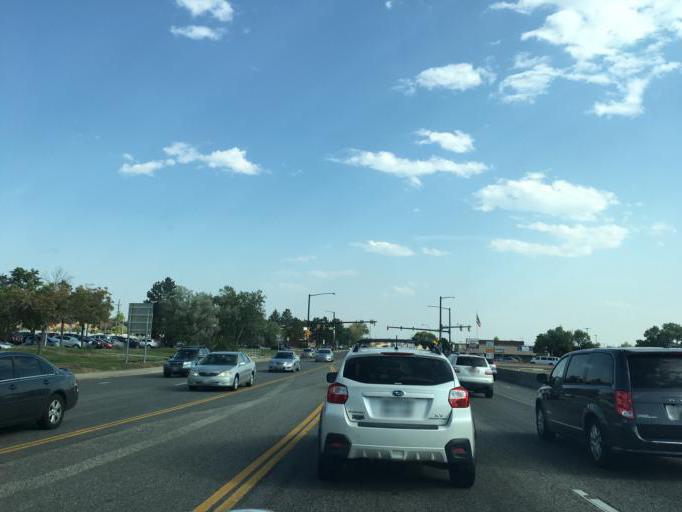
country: US
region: Colorado
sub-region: Adams County
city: Westminster
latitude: 39.8574
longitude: -105.0554
